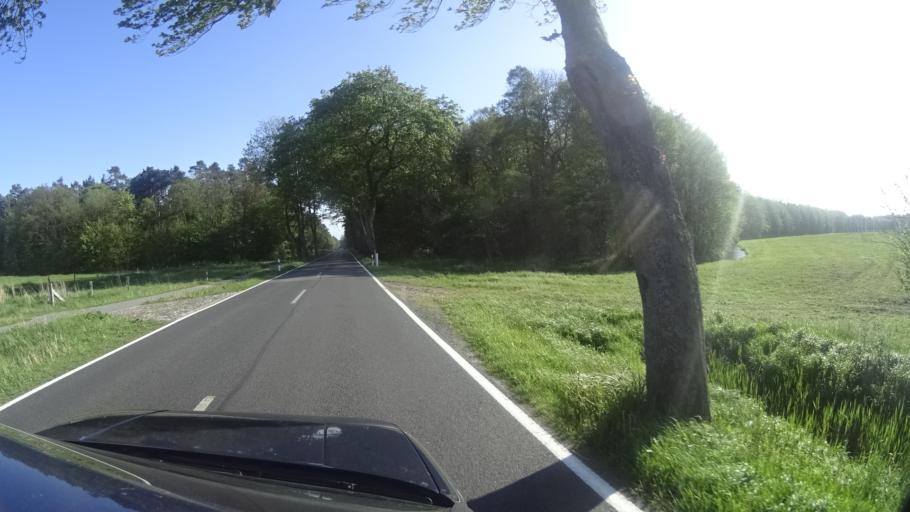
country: DE
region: Mecklenburg-Vorpommern
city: Ostseebad Prerow
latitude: 54.4336
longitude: 12.5756
